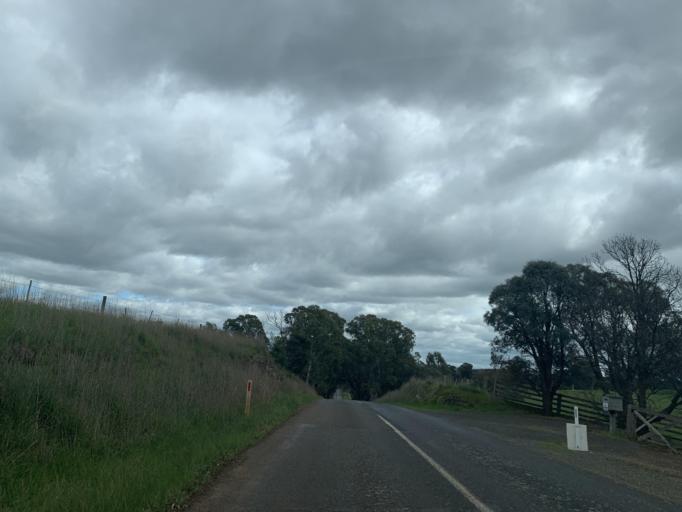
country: AU
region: Victoria
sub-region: Whittlesea
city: Whittlesea
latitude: -37.1859
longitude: 145.0188
